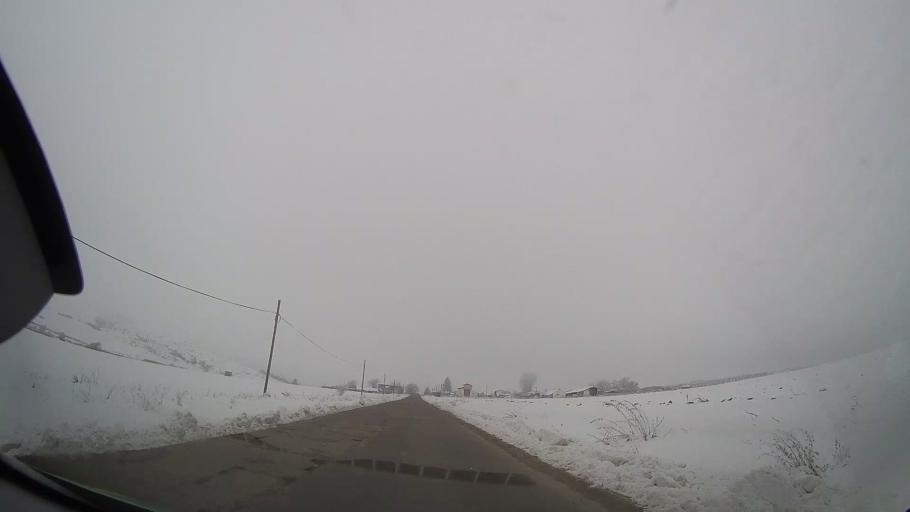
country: RO
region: Neamt
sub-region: Comuna Icusesti
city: Balusesti
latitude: 46.8558
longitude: 27.0314
